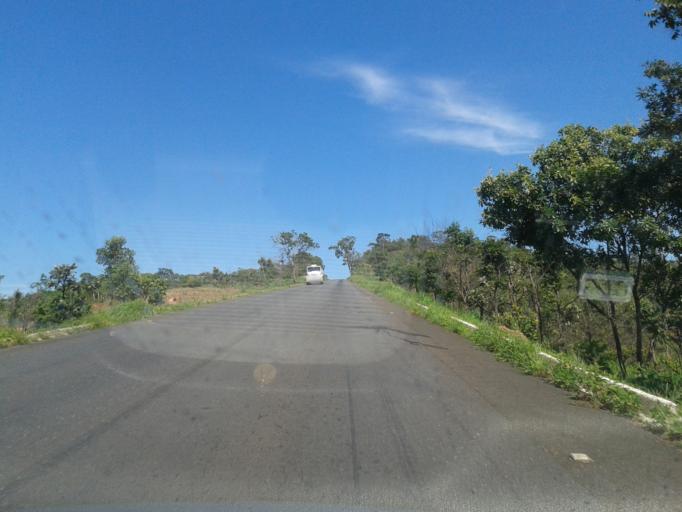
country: BR
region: Goias
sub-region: Bela Vista De Goias
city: Bela Vista de Goias
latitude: -17.1537
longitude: -48.7984
